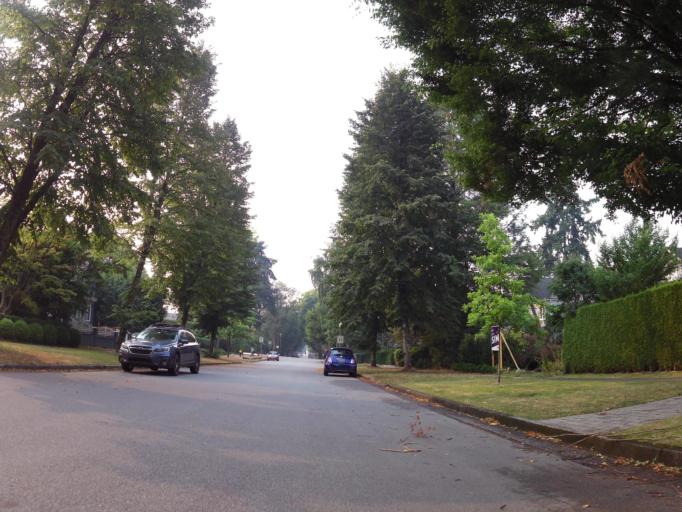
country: CA
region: British Columbia
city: Vancouver
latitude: 49.2281
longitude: -123.1479
